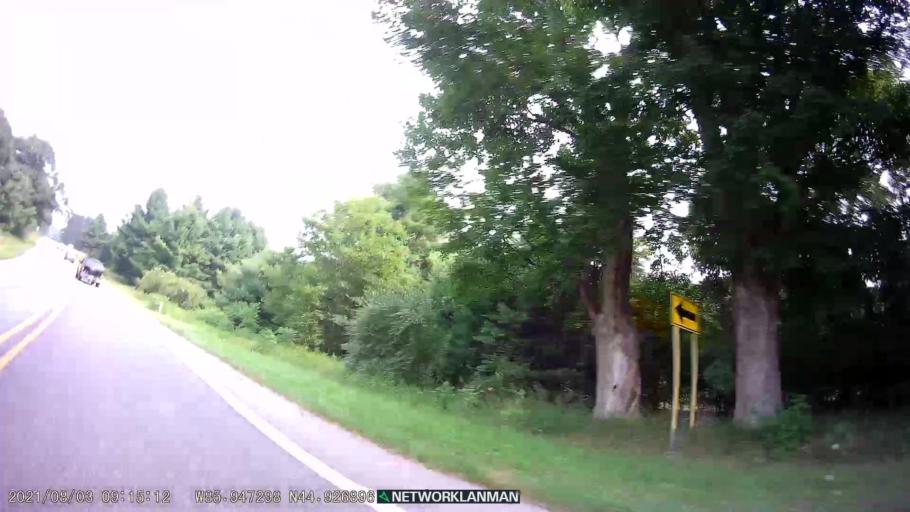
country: US
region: Michigan
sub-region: Leelanau County
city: Leland
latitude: 44.9270
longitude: -85.9473
